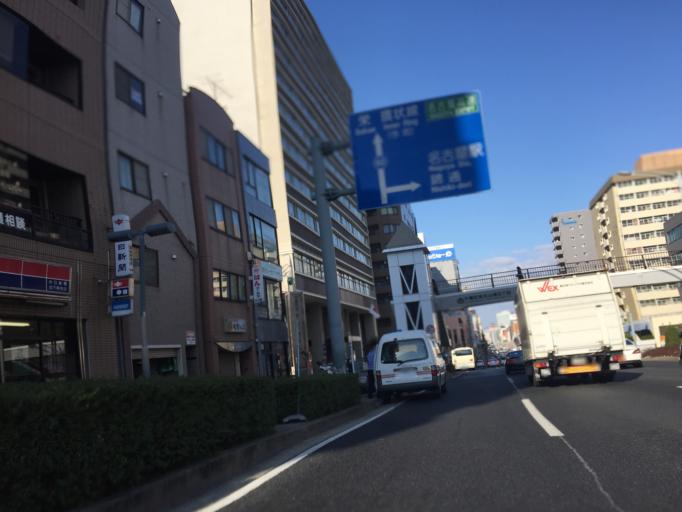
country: JP
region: Aichi
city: Nagoya-shi
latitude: 35.1667
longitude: 136.9469
